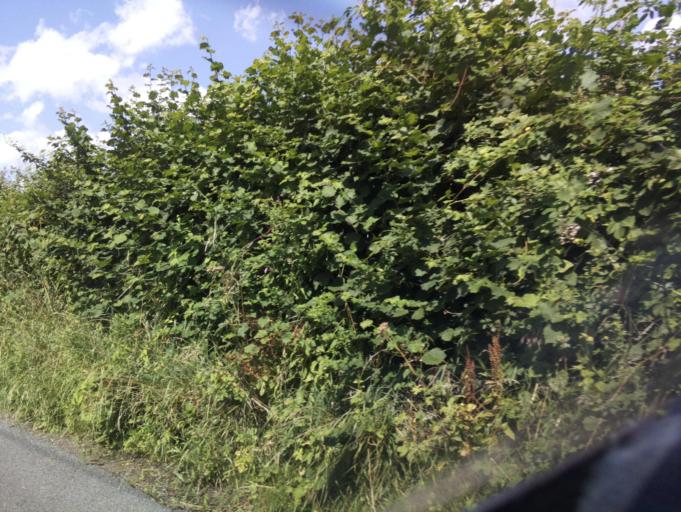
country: GB
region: England
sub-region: Hampshire
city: Kingsclere
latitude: 51.3458
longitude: -1.2813
